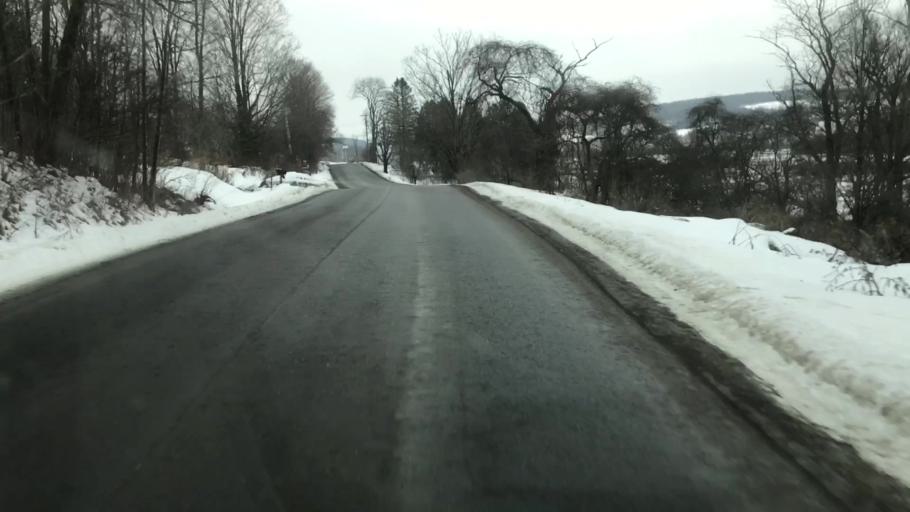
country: US
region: New York
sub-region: Cortland County
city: Cortland West
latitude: 42.6638
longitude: -76.2773
